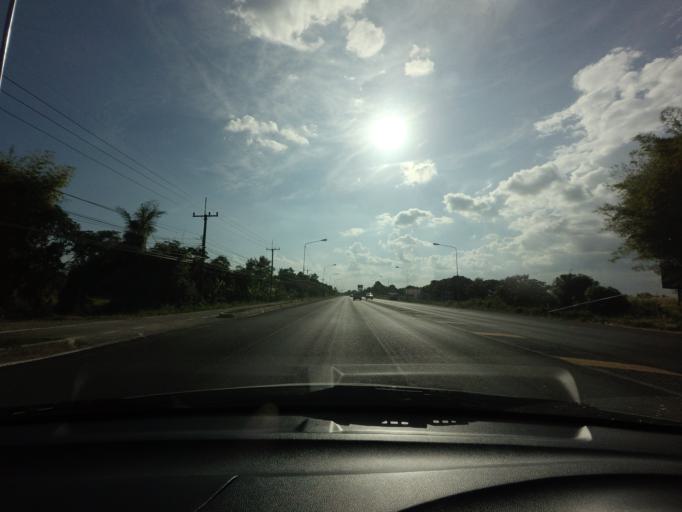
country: TH
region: Nakhon Nayok
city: Nakhon Nayok
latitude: 14.2495
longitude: 101.2554
